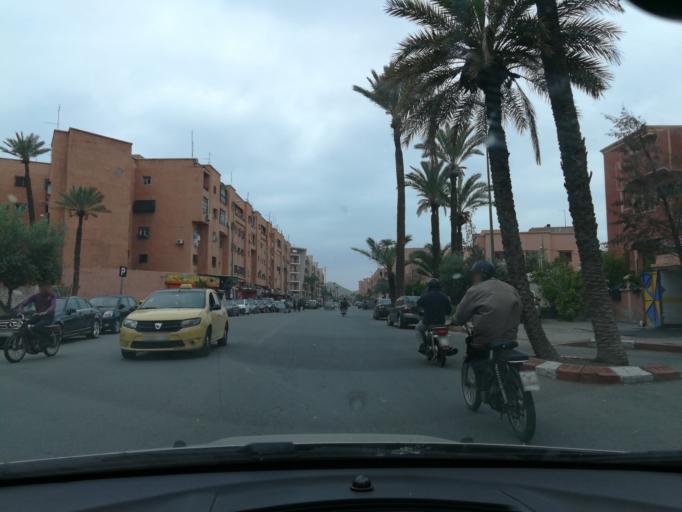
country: MA
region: Marrakech-Tensift-Al Haouz
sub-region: Marrakech
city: Marrakesh
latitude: 31.6489
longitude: -8.0077
